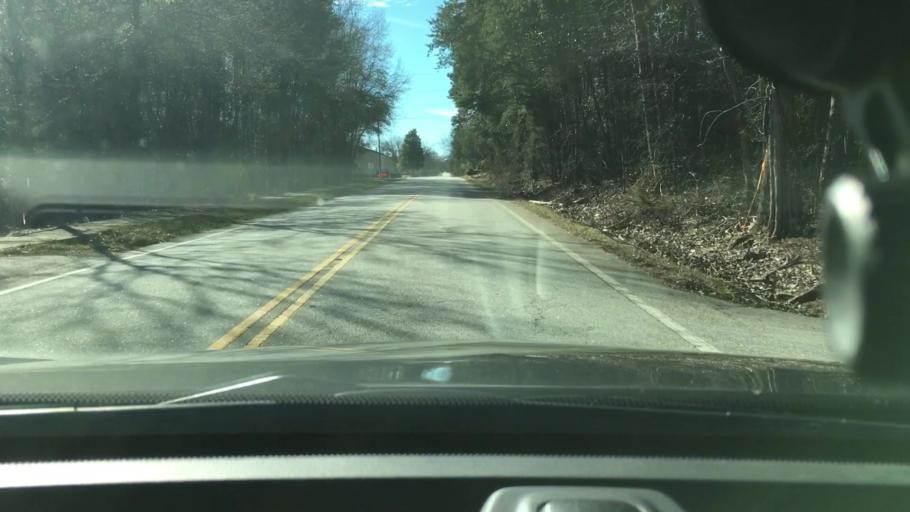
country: US
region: South Carolina
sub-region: Spartanburg County
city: Pacolet
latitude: 34.9129
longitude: -81.7687
